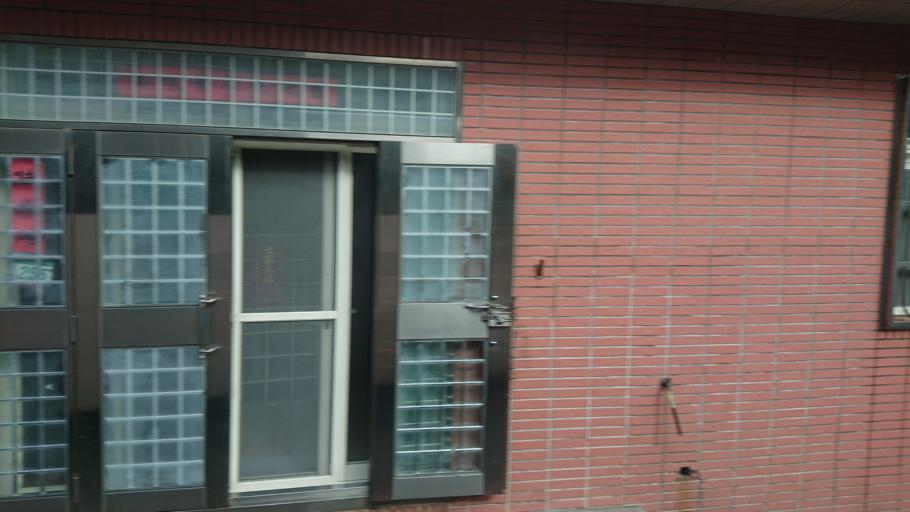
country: TW
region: Taiwan
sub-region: Keelung
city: Keelung
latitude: 25.1069
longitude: 121.8539
